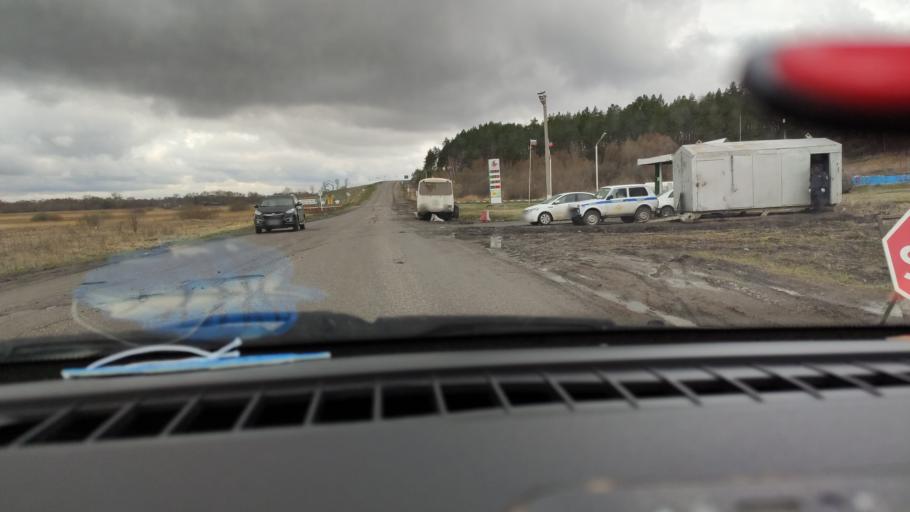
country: RU
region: Tatarstan
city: Nurlat
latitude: 54.3853
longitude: 50.7452
